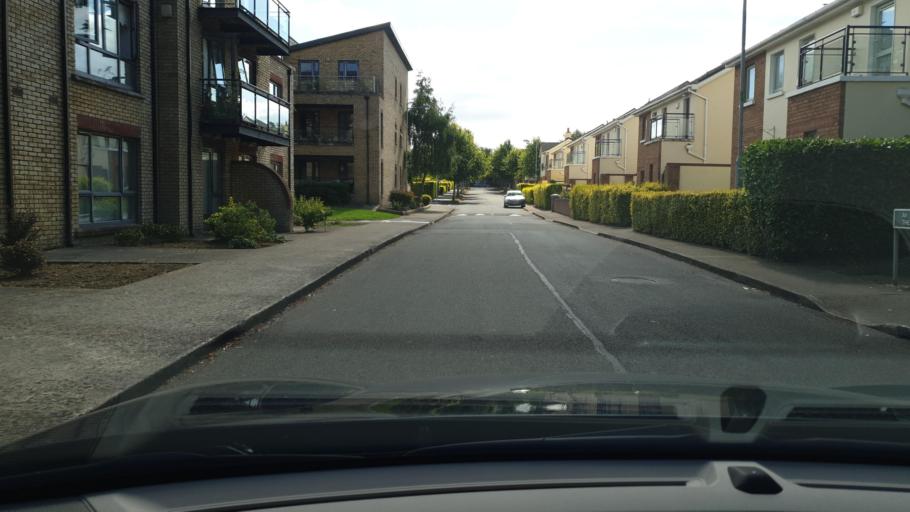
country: IE
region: Leinster
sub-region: An Mhi
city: Dunboyne
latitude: 53.4156
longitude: -6.4801
